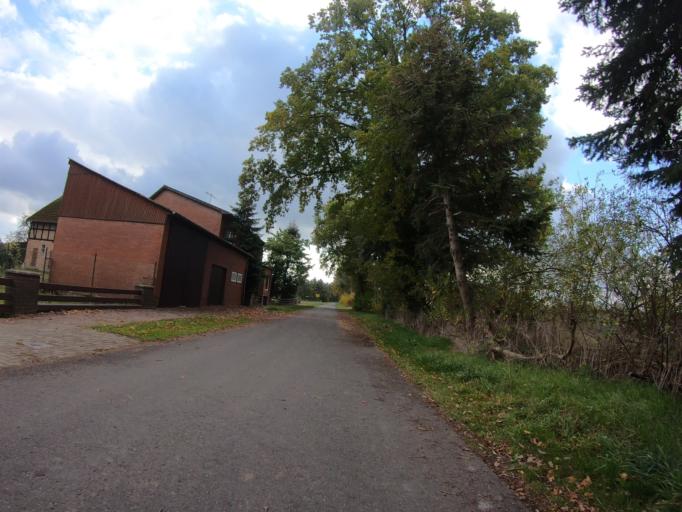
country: DE
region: Lower Saxony
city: Wahrenholz
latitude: 52.6062
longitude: 10.6074
